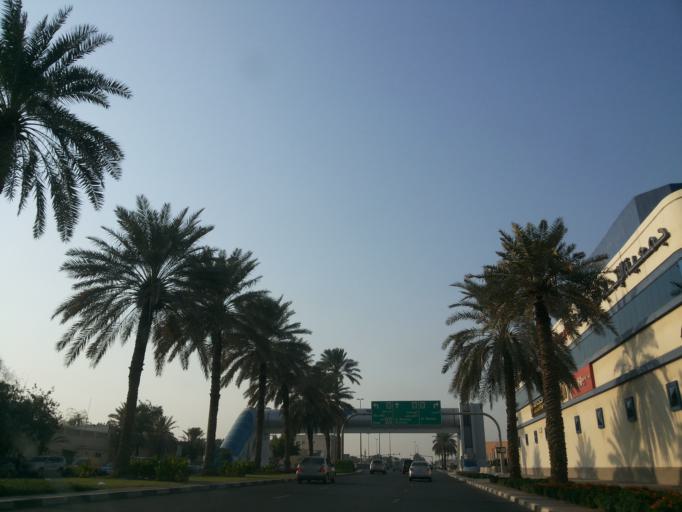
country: AE
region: Ash Shariqah
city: Sharjah
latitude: 25.2821
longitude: 55.3409
